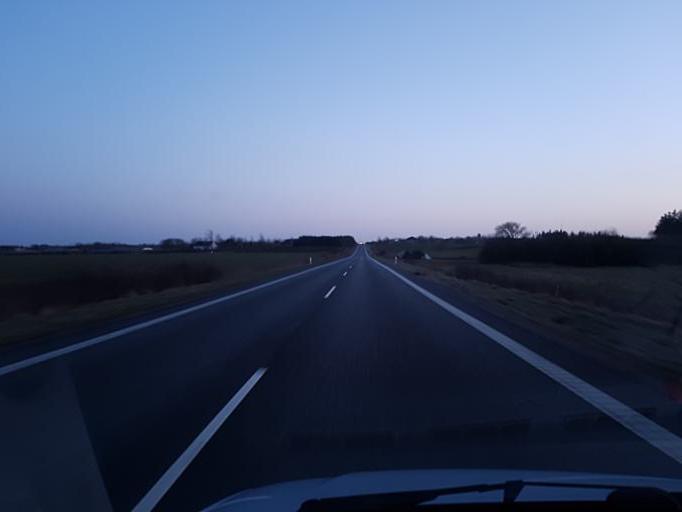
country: DK
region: Central Jutland
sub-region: Ringkobing-Skjern Kommune
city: Videbaek
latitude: 56.2081
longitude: 8.5840
